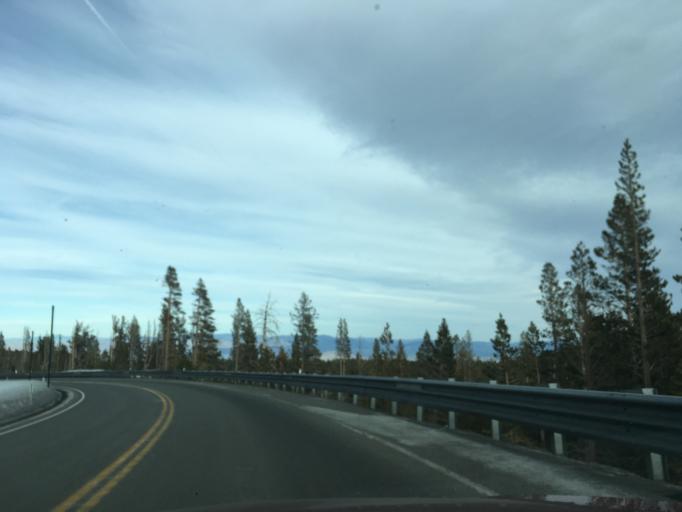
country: US
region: Nevada
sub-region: Washoe County
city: Incline Village
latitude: 39.3180
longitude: -119.9019
